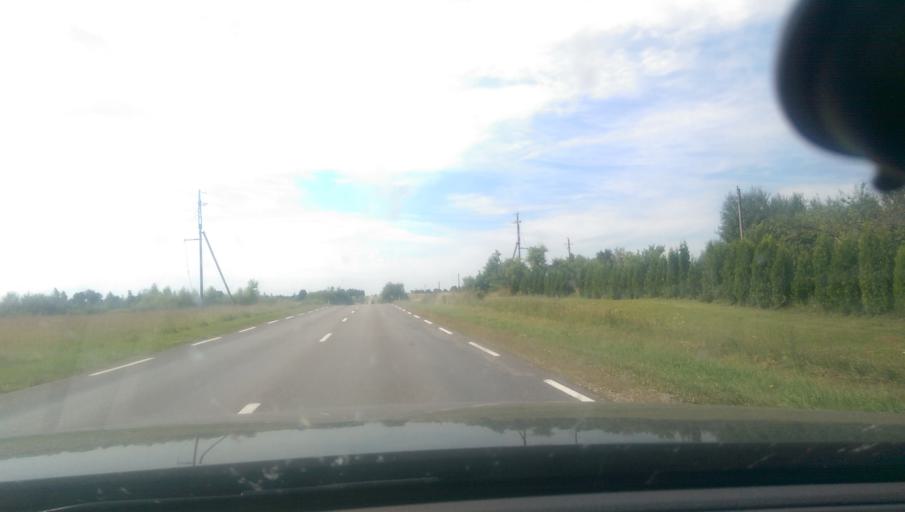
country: LT
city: Jieznas
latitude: 54.6624
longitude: 24.1889
